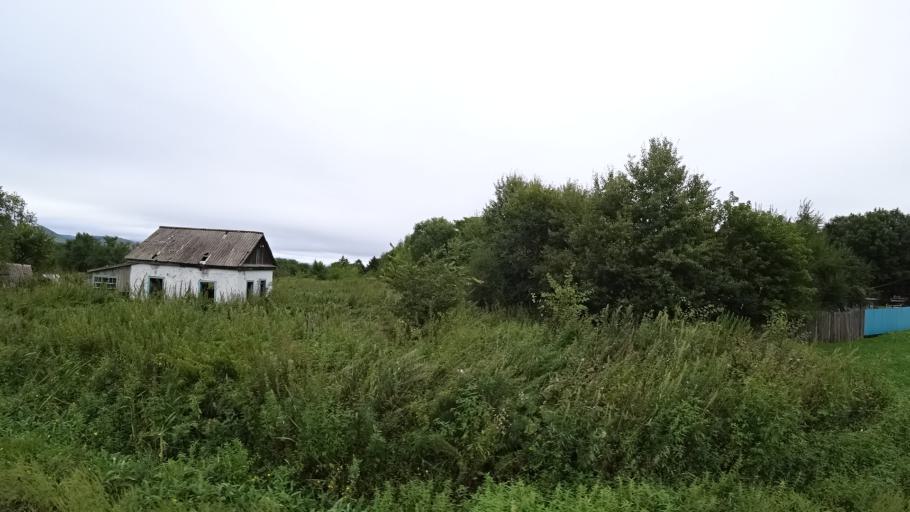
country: RU
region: Primorskiy
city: Monastyrishche
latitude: 44.0901
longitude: 132.5731
